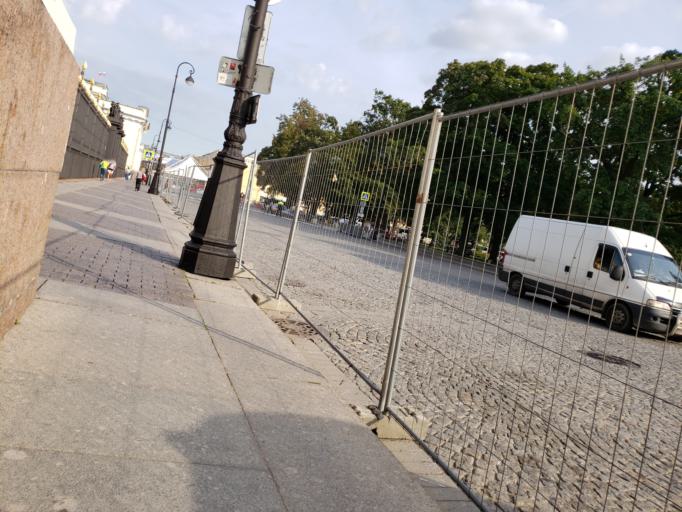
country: RU
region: St.-Petersburg
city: Saint Petersburg
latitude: 59.9381
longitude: 30.3308
